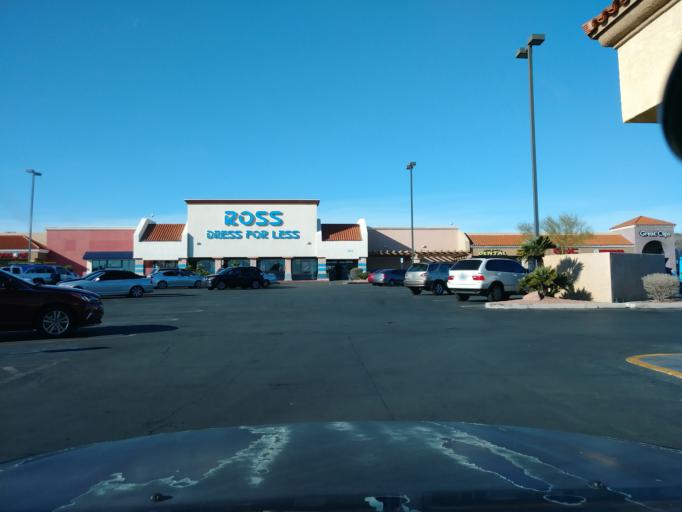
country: US
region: Nevada
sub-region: Clark County
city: Spring Valley
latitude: 36.1614
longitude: -115.2443
